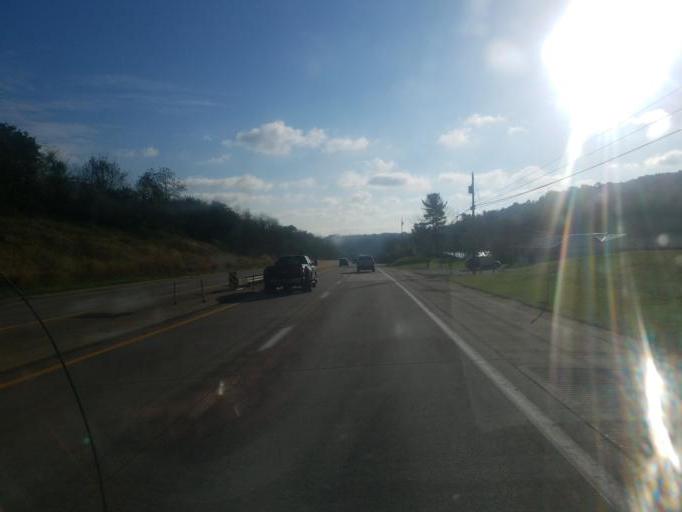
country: US
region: Pennsylvania
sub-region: Westmoreland County
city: Delmont
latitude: 40.3982
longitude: -79.5011
